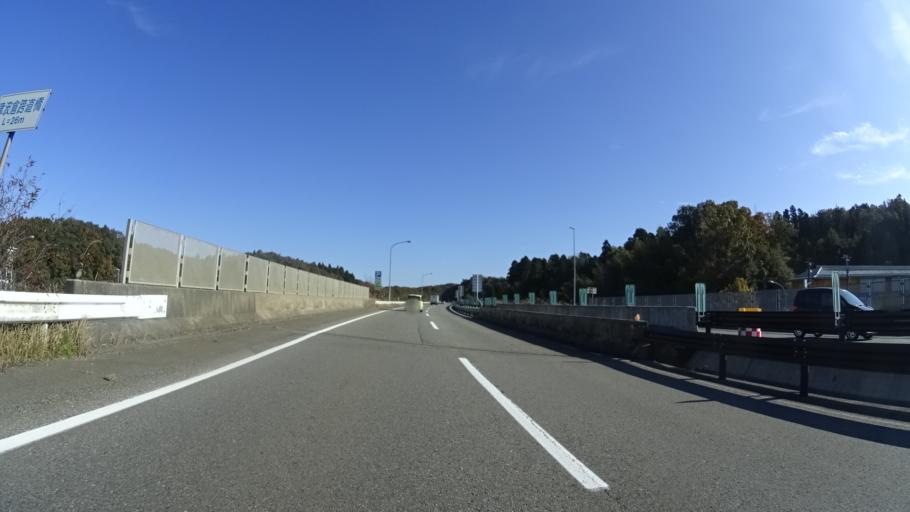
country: JP
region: Ishikawa
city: Komatsu
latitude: 36.3413
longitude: 136.4440
